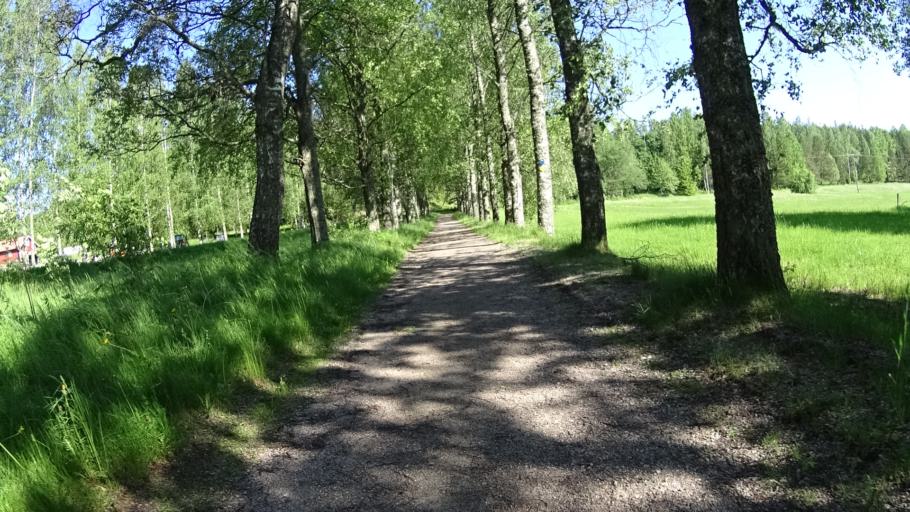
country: FI
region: Uusimaa
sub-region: Helsinki
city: Kauniainen
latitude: 60.3175
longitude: 24.6913
